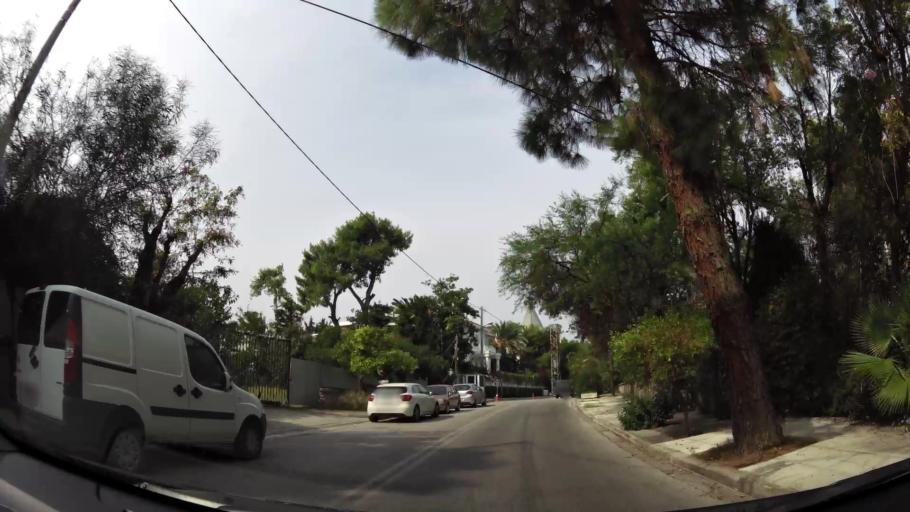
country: GR
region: Attica
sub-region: Nomarchia Athinas
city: Psychiko
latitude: 38.0067
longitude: 23.7727
